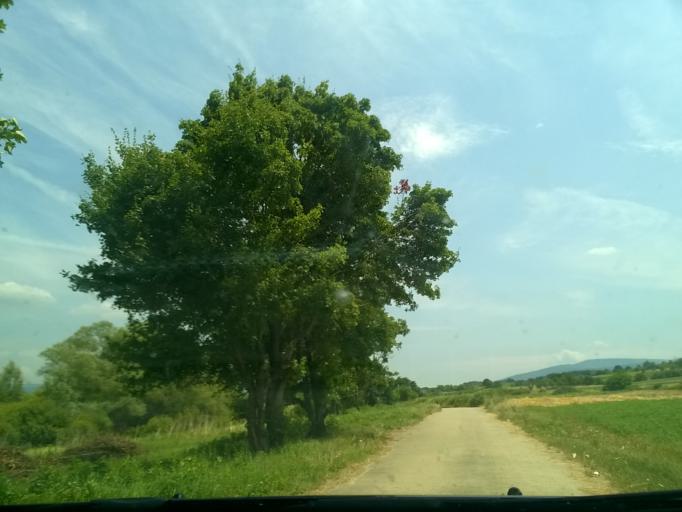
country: RS
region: Central Serbia
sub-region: Zajecarski Okrug
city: Soko Banja
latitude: 43.6530
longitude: 21.7627
